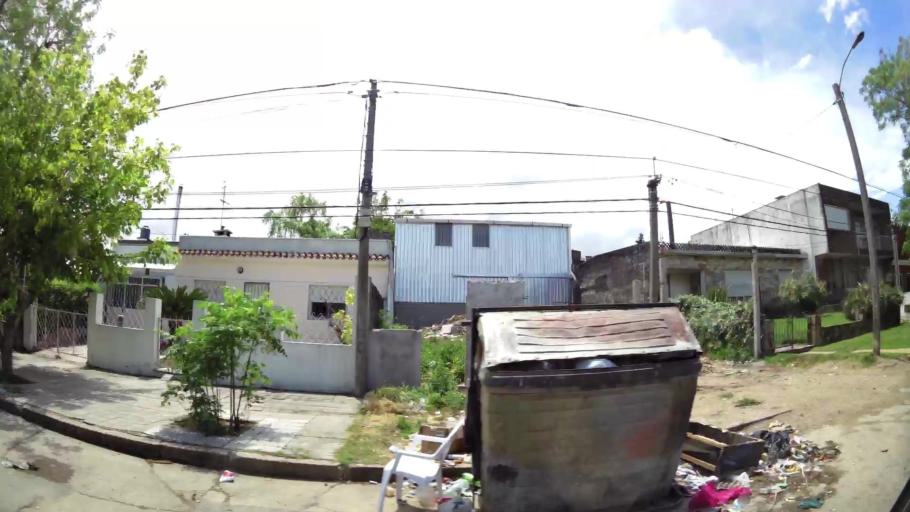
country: UY
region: Montevideo
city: Montevideo
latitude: -34.8776
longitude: -56.1288
